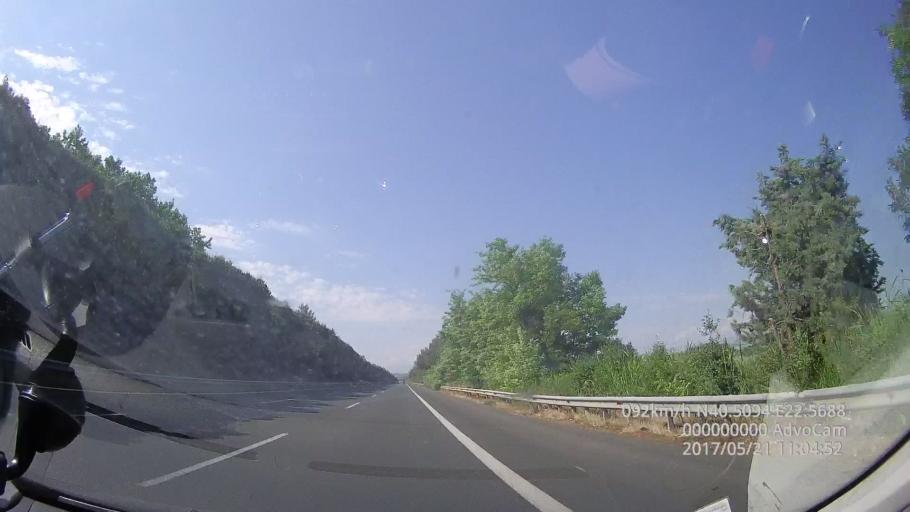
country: GR
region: Central Macedonia
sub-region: Nomos Pierias
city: Aiginio
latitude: 40.5089
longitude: 22.5686
